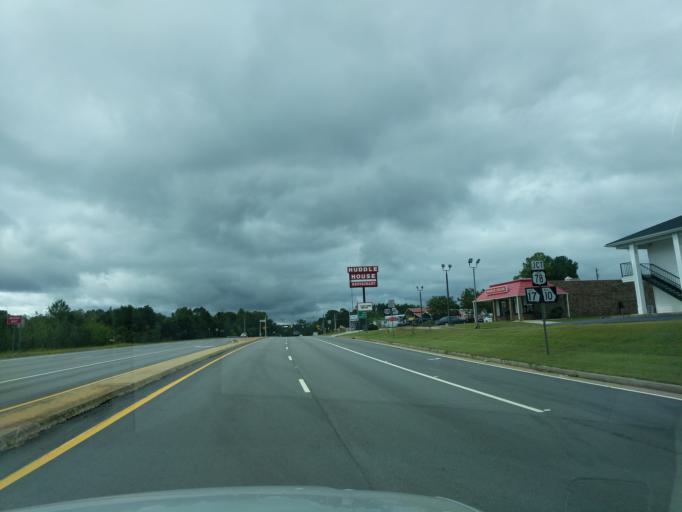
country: US
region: Georgia
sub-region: Wilkes County
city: Washington
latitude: 33.7293
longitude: -82.7155
